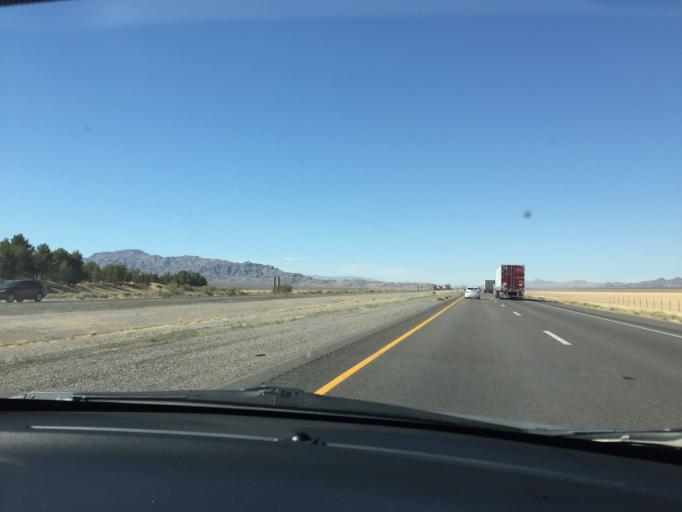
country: US
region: Nevada
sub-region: Clark County
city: Sandy Valley
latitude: 35.5529
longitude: -115.4144
